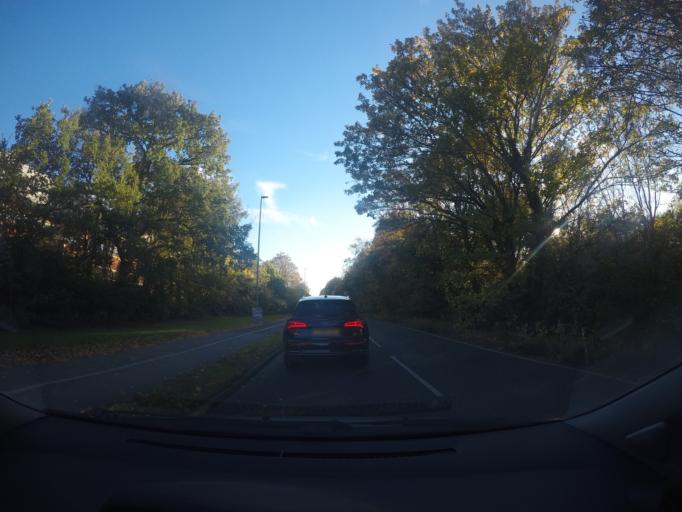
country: GB
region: England
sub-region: City of York
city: York
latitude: 53.9770
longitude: -1.0819
